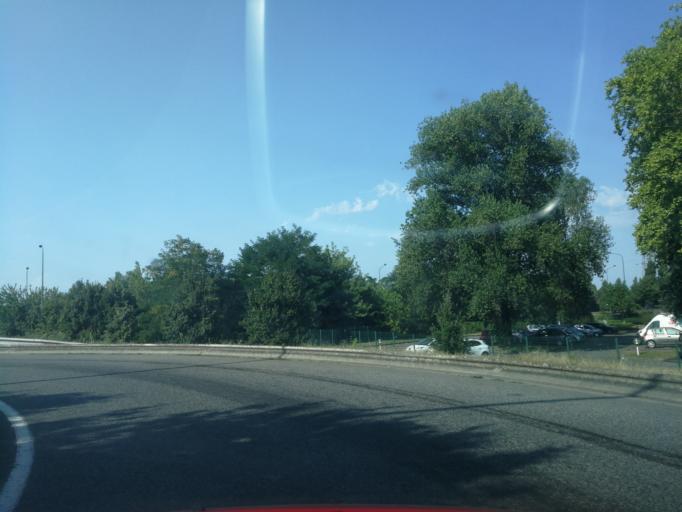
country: FR
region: Midi-Pyrenees
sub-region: Departement de la Haute-Garonne
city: Blagnac
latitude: 43.6243
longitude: 1.4115
